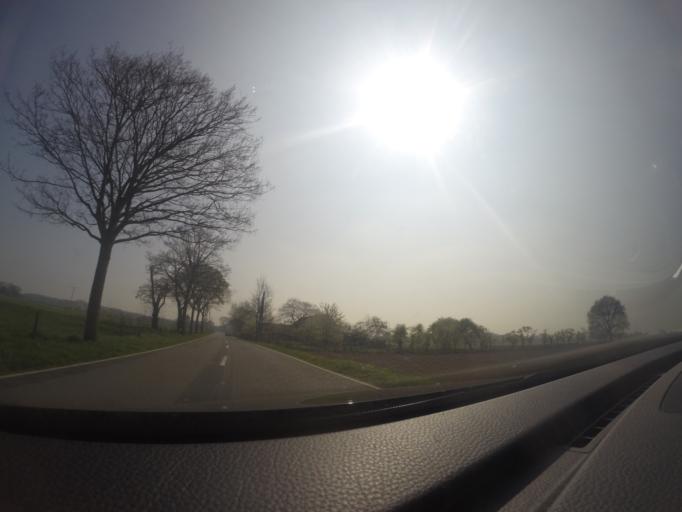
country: DE
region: North Rhine-Westphalia
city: Rees
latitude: 51.8081
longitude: 6.4145
